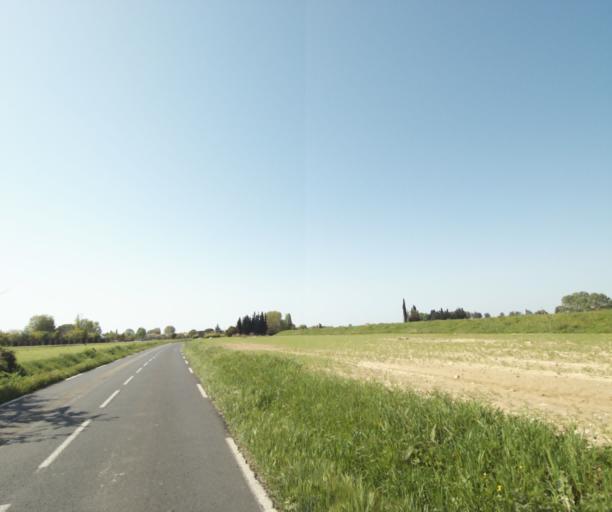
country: FR
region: Languedoc-Roussillon
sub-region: Departement de l'Herault
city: Lattes
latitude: 43.5833
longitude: 3.9088
